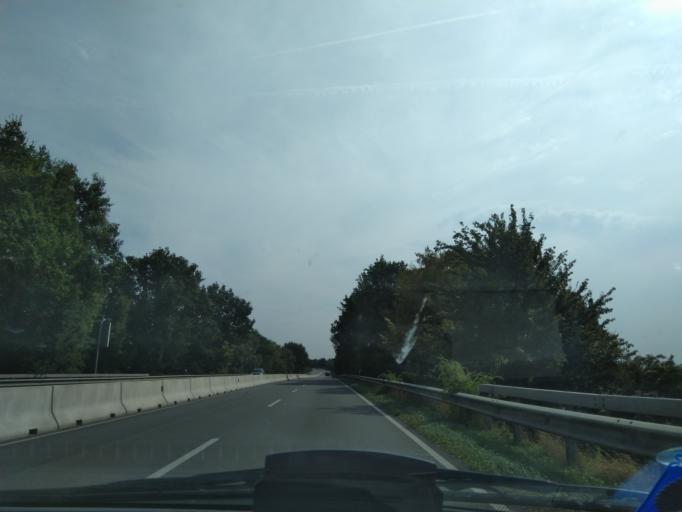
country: DE
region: Lower Saxony
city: Meppen
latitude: 52.6910
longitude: 7.2818
